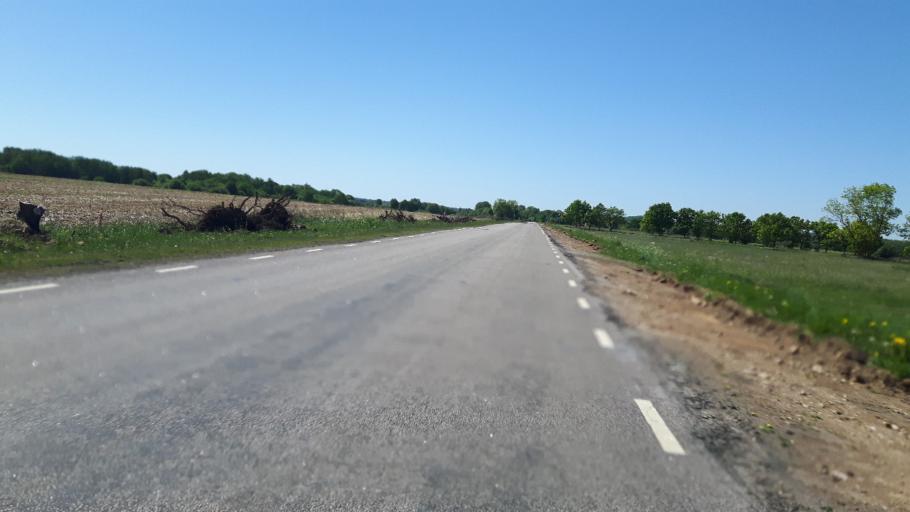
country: EE
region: Ida-Virumaa
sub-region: Narva-Joesuu linn
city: Narva-Joesuu
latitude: 59.3988
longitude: 27.9320
